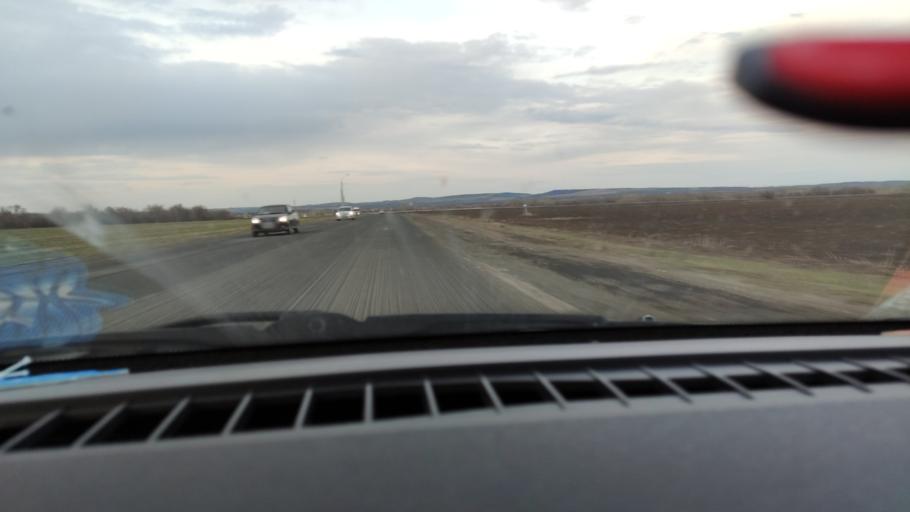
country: RU
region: Saratov
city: Yelshanka
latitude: 51.8148
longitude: 46.2088
